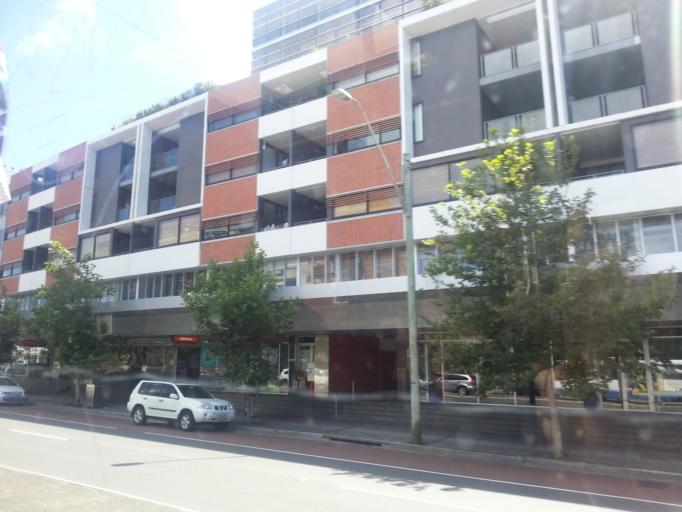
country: AU
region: New South Wales
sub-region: Randwick
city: Kensington
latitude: -33.9125
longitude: 151.2238
